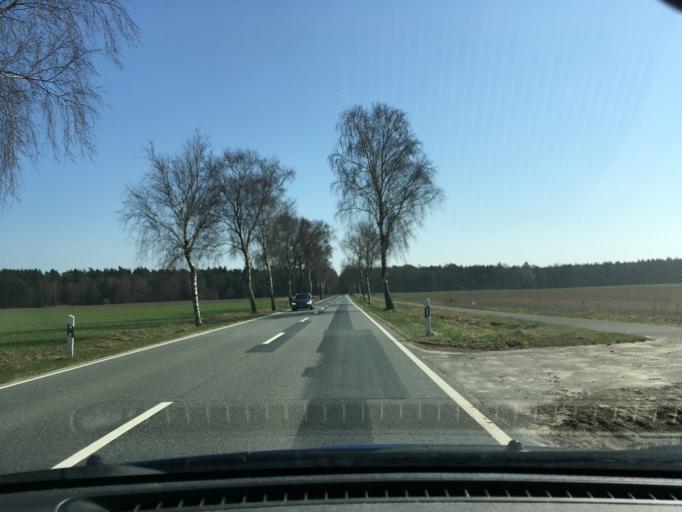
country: DE
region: Lower Saxony
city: Rehlingen
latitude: 53.0949
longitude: 10.2632
